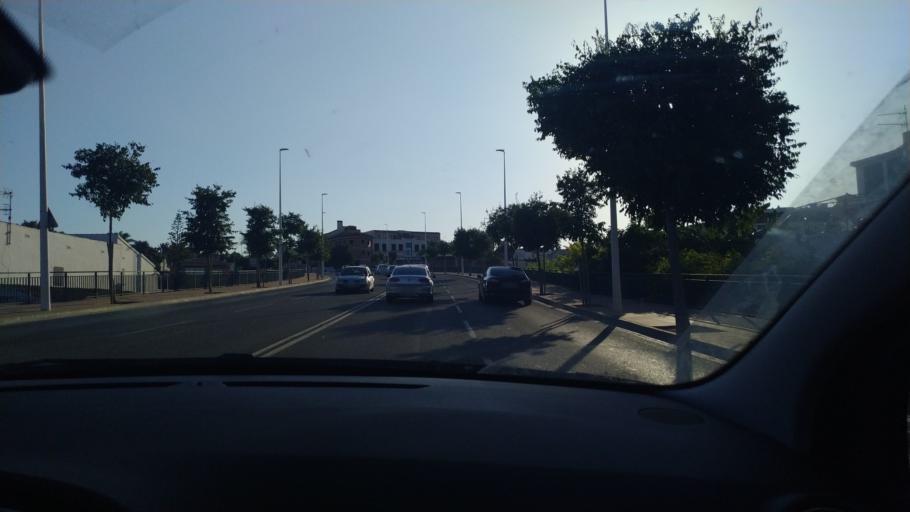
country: ES
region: Valencia
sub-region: Provincia de Alicante
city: Javea
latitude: 38.7855
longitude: 0.1619
